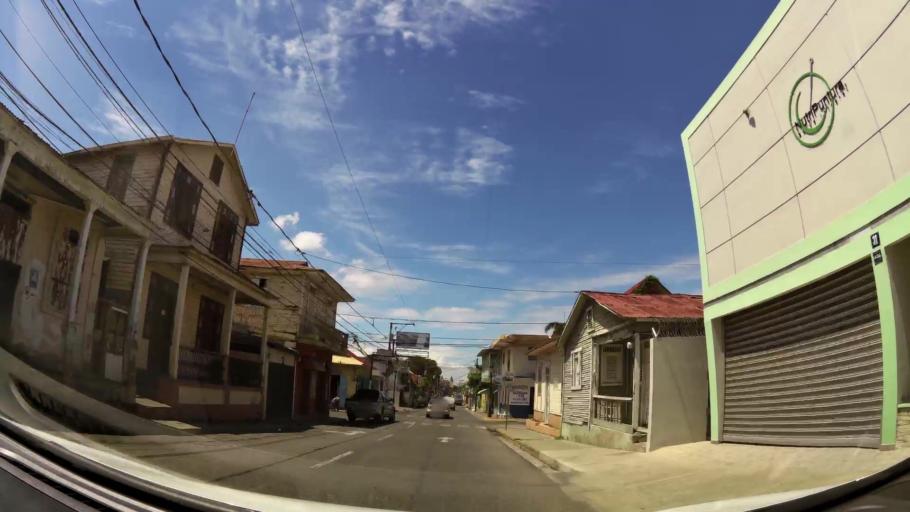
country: DO
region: Santiago
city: Santiago de los Caballeros
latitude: 19.4490
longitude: -70.6993
